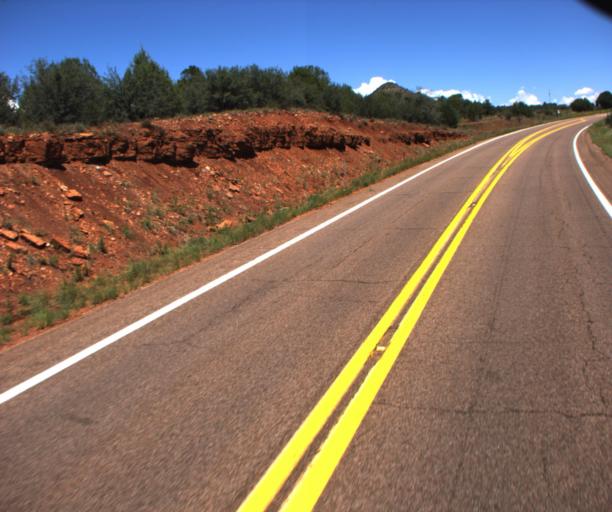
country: US
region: Arizona
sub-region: Navajo County
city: Cibecue
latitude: 33.9550
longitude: -110.3318
